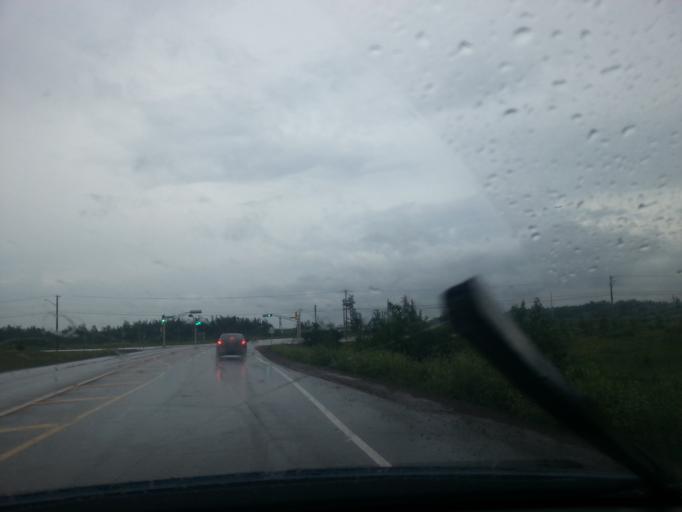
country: CA
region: New Brunswick
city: Dieppe
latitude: 46.1235
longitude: -64.7241
